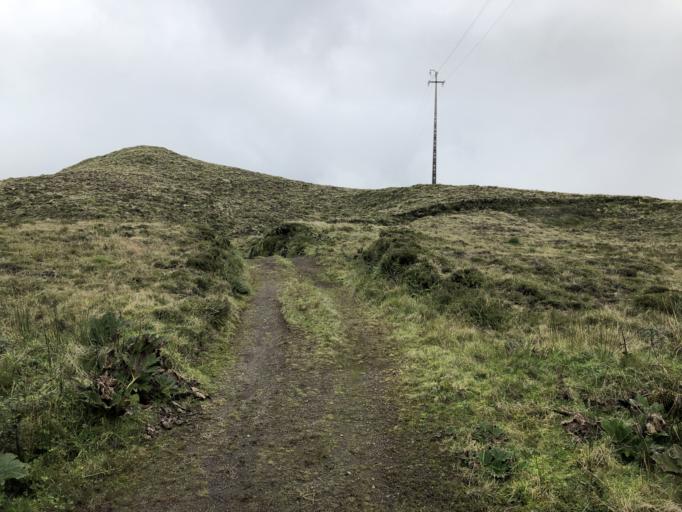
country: PT
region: Azores
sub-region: Ponta Delgada
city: Arrifes
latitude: 37.8317
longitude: -25.7577
